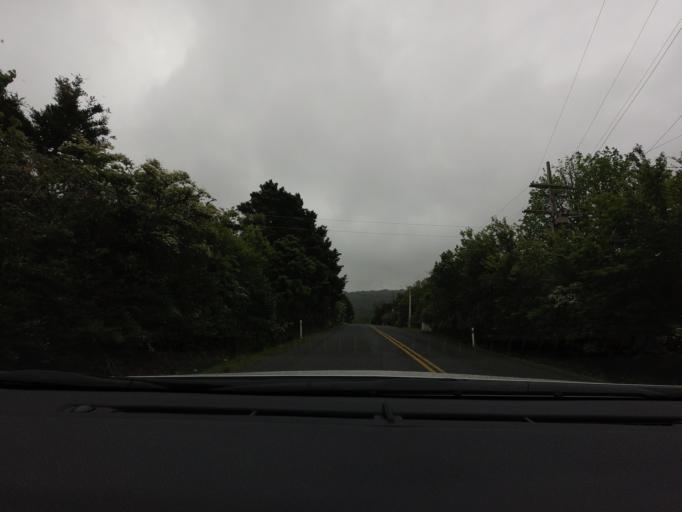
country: NZ
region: Auckland
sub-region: Auckland
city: Warkworth
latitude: -36.2825
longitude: 174.6421
